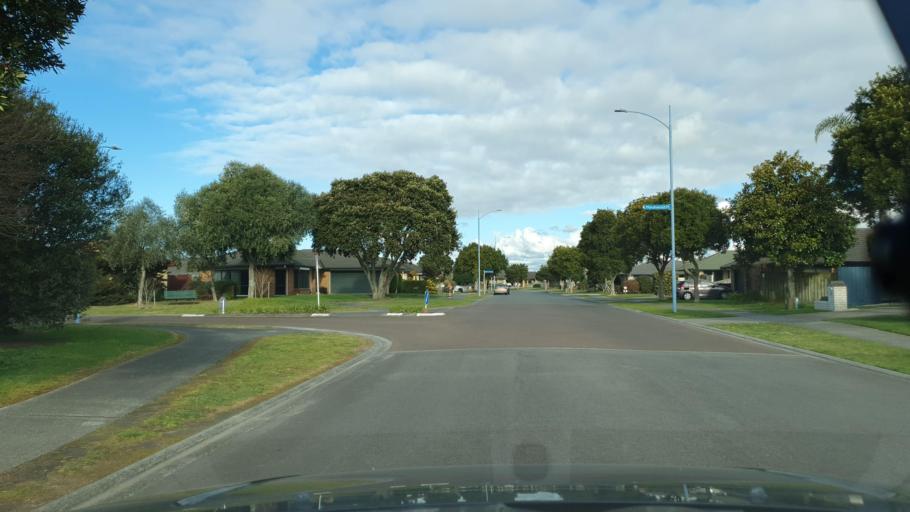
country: NZ
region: Bay of Plenty
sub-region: Tauranga City
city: Tauranga
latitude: -37.7081
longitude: 176.2899
